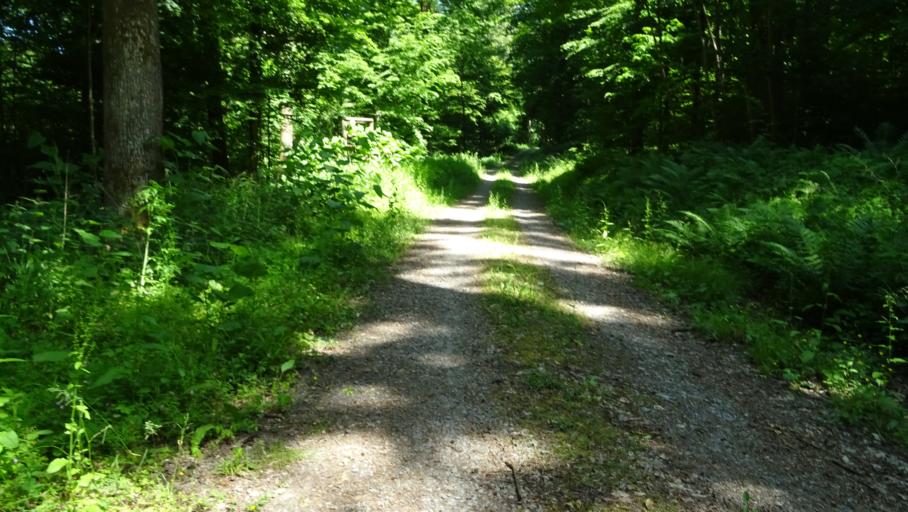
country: DE
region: Baden-Wuerttemberg
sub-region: Karlsruhe Region
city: Obrigheim
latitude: 49.3294
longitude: 9.0632
